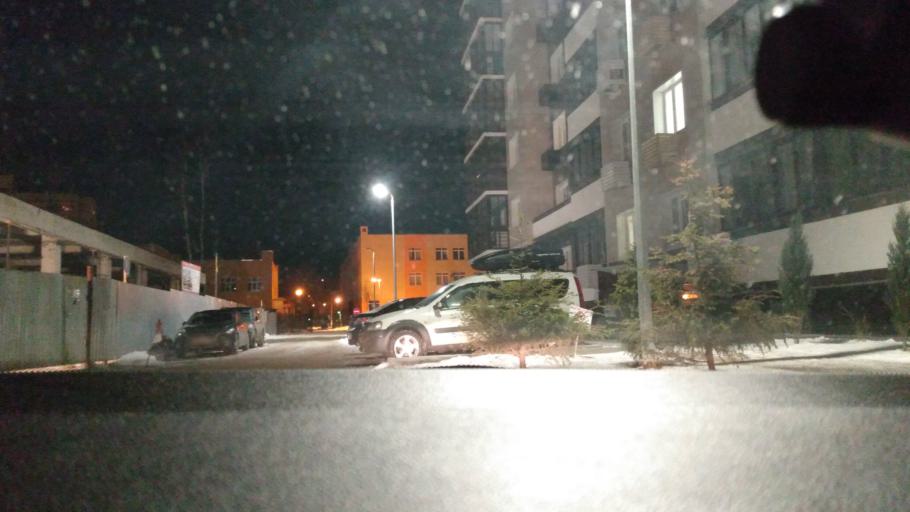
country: RU
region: Moskovskaya
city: Pushkino
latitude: 56.0129
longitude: 37.8525
